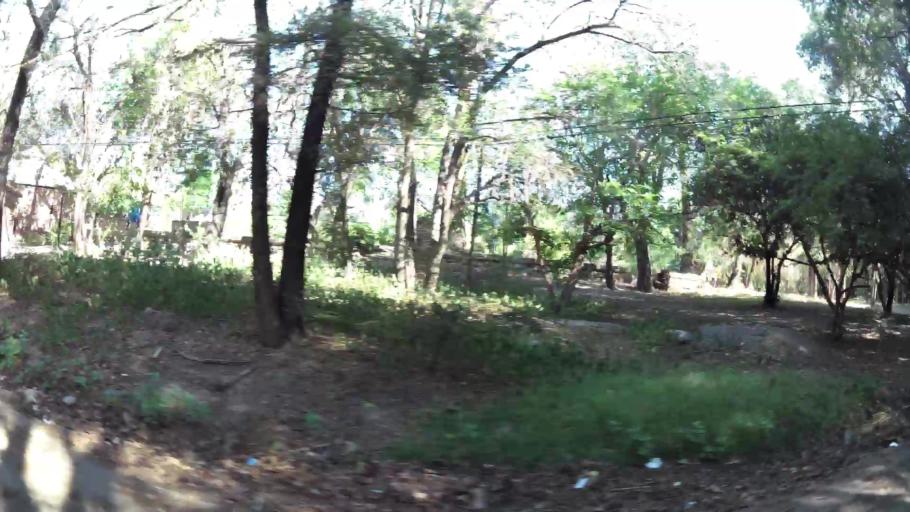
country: AR
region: Mendoza
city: Mendoza
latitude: -32.8879
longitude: -68.8702
